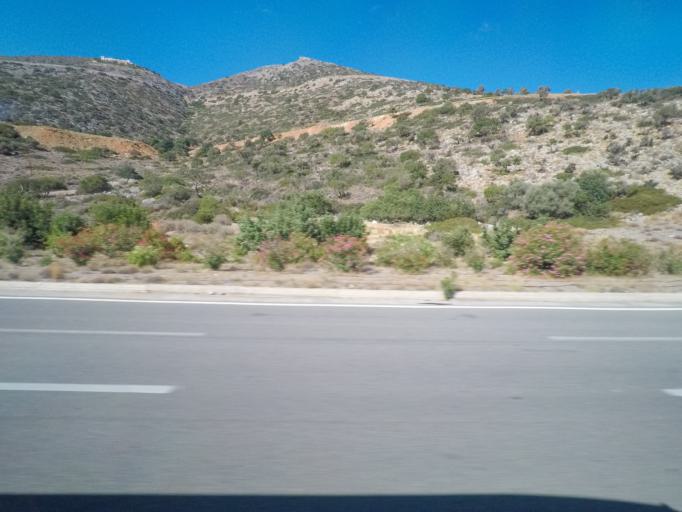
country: GR
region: Crete
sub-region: Nomos Irakleiou
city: Stalis
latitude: 35.2857
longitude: 25.4243
